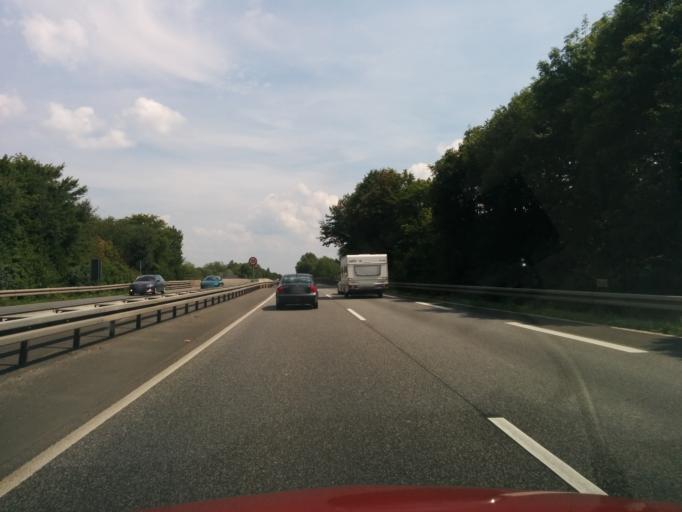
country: DE
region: Hesse
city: Allendorf an der Lahn
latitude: 50.5691
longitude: 8.5692
